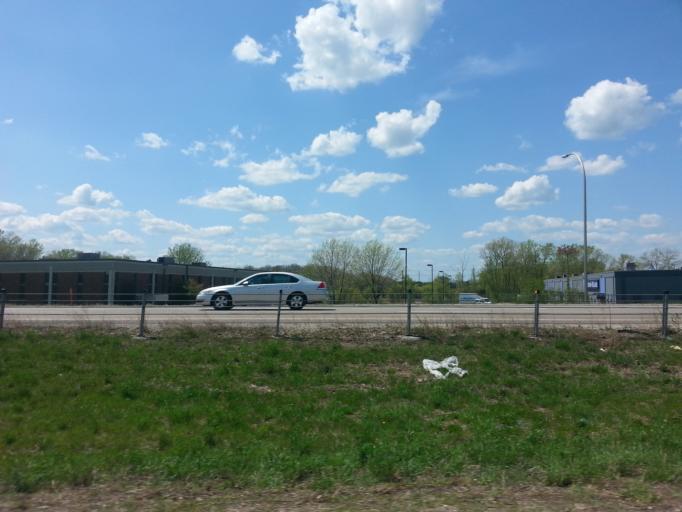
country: US
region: Minnesota
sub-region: Hennepin County
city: Edina
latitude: 44.8636
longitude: -93.3960
